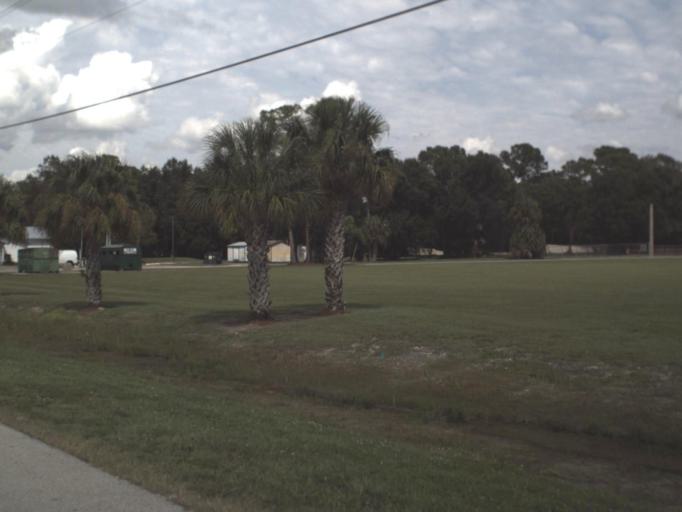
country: US
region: Florida
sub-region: Hendry County
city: LaBelle
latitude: 26.7423
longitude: -81.4378
